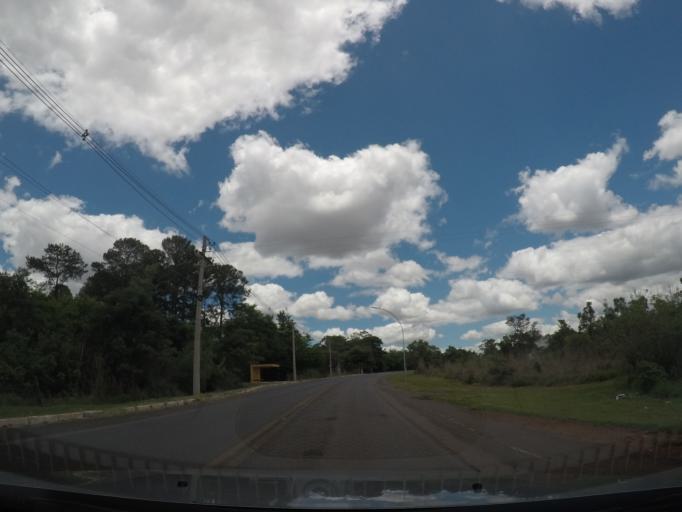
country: BR
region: Federal District
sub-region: Brasilia
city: Brasilia
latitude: -15.7732
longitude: -47.8129
